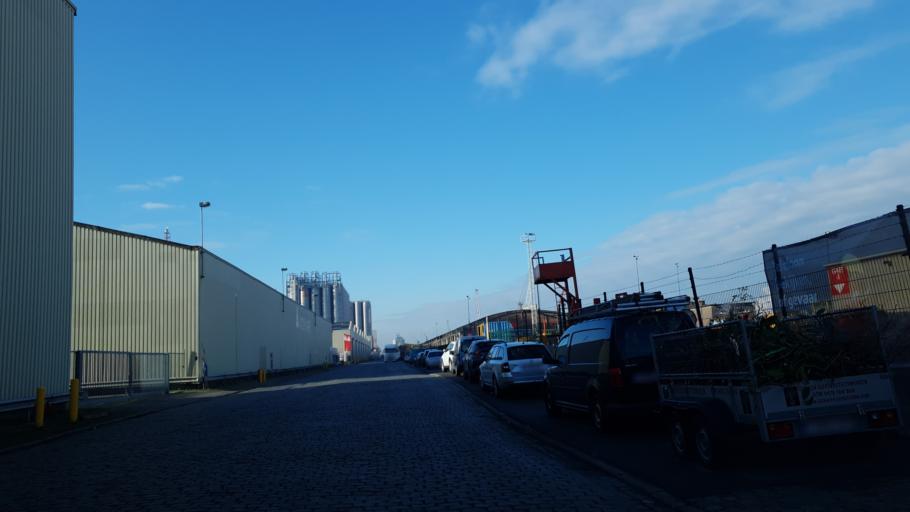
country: BE
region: Flanders
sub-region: Provincie Antwerpen
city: Antwerpen
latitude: 51.2450
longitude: 4.3778
